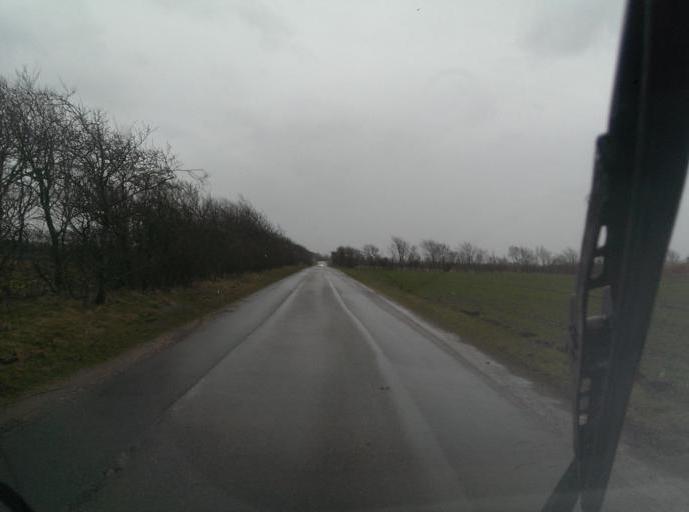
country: DK
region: Central Jutland
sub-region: Ringkobing-Skjern Kommune
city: Skjern
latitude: 56.0117
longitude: 8.4177
